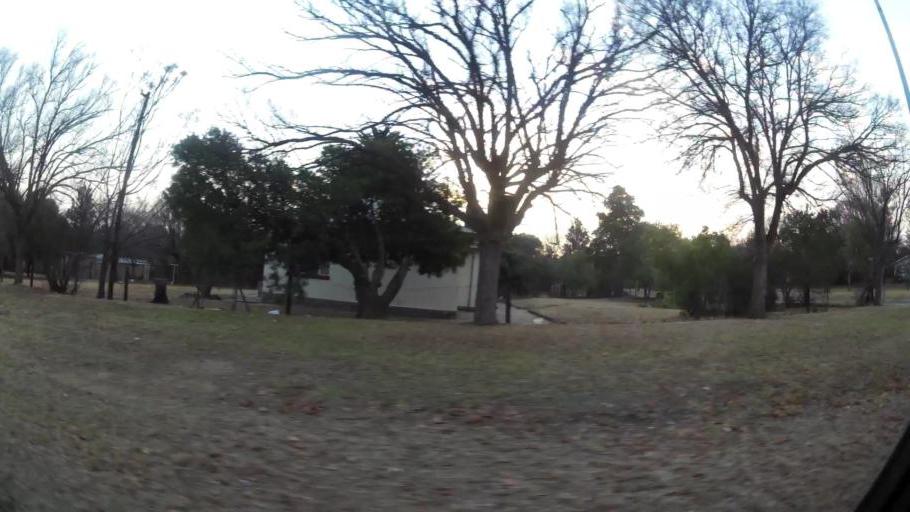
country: ZA
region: Gauteng
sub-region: City of Johannesburg Metropolitan Municipality
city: Diepsloot
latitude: -26.0055
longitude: 28.0457
